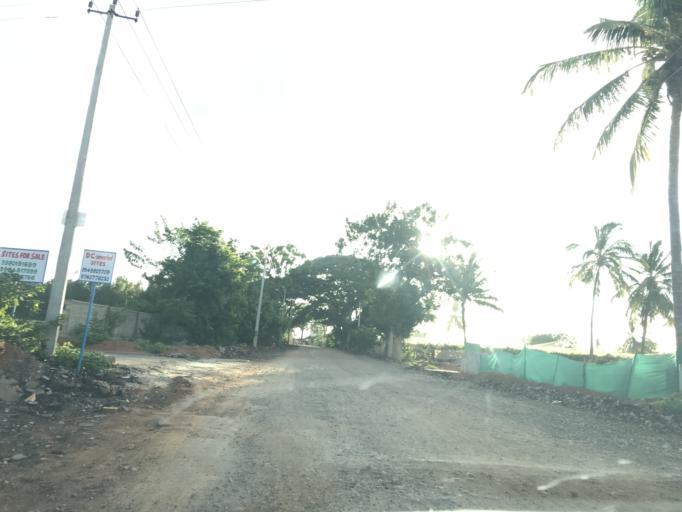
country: IN
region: Karnataka
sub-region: Bangalore Urban
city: Yelahanka
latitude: 13.1314
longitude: 77.6995
